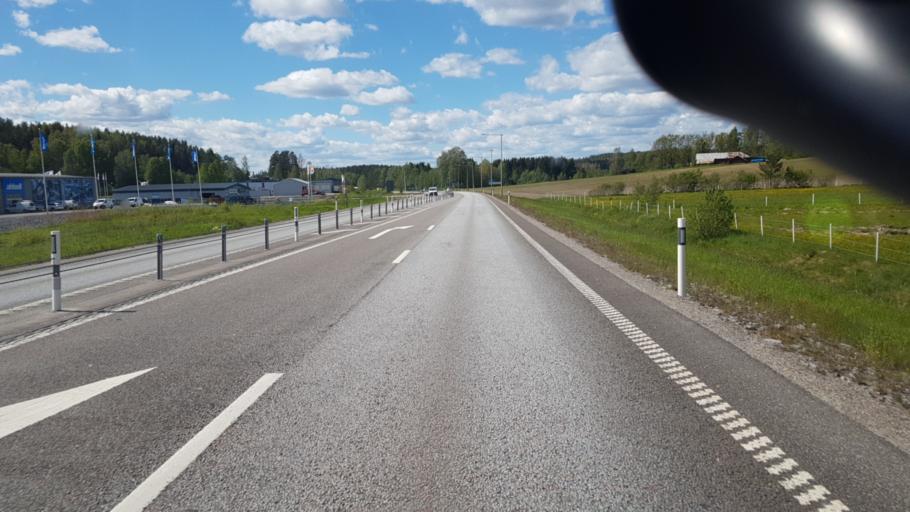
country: SE
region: Vaermland
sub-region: Arvika Kommun
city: Arvika
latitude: 59.6583
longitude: 12.6433
